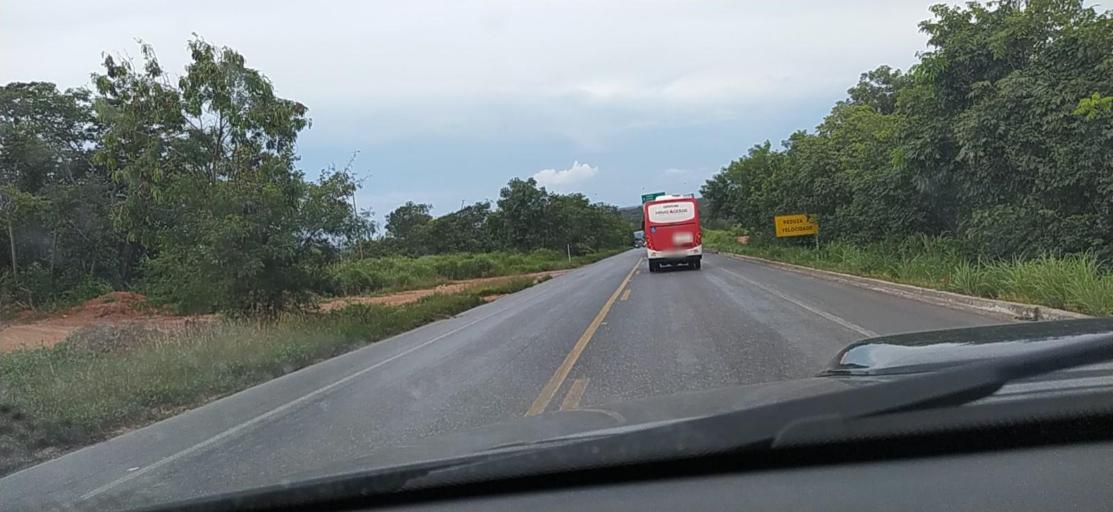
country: BR
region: Minas Gerais
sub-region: Montes Claros
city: Montes Claros
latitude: -16.6677
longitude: -43.7883
